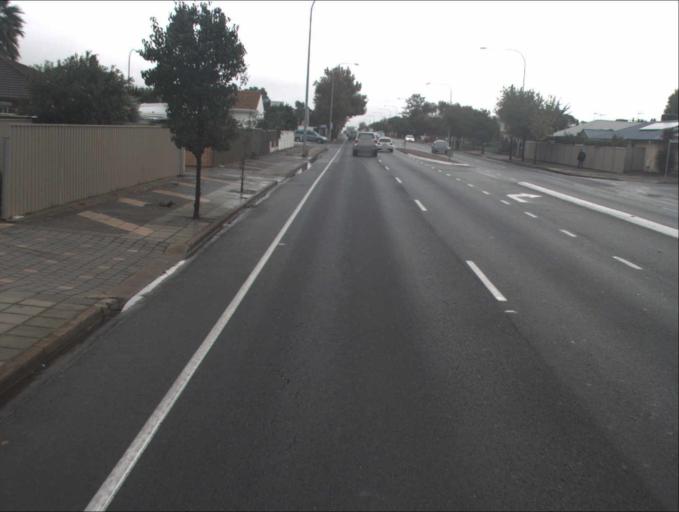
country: AU
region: South Australia
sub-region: Port Adelaide Enfield
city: Enfield
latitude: -34.8566
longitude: 138.6180
